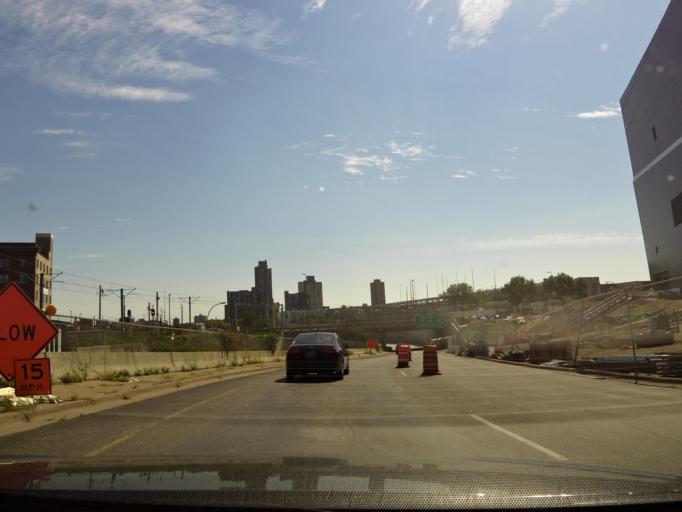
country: US
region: Minnesota
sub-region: Hennepin County
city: Minneapolis
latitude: 44.9744
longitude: -93.2558
